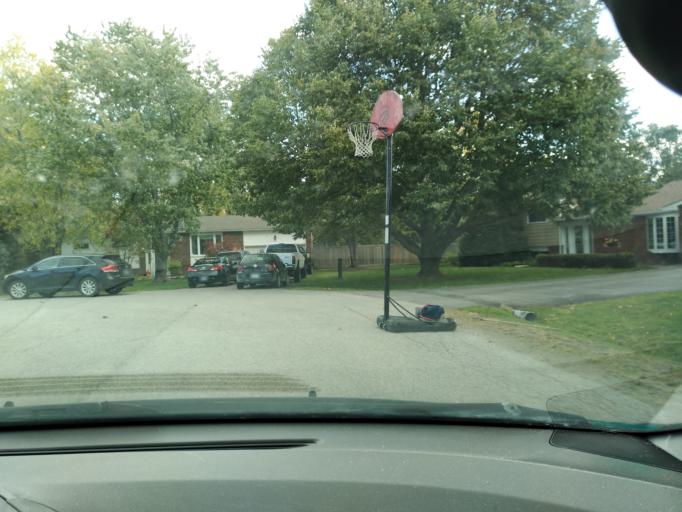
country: CA
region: Ontario
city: Bradford West Gwillimbury
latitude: 44.0879
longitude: -79.6798
